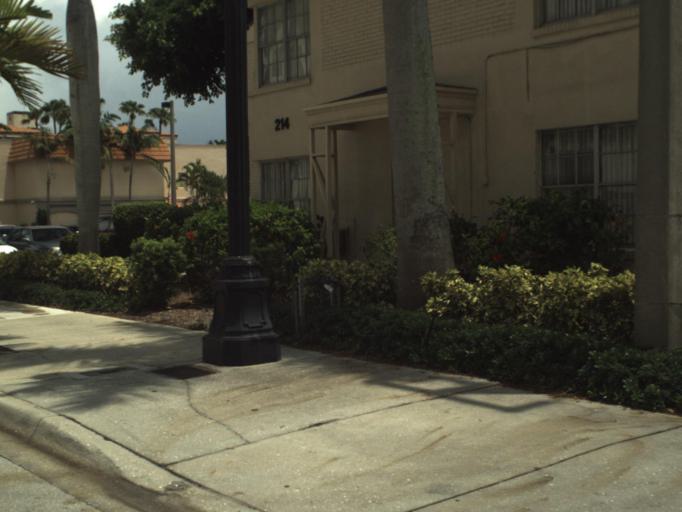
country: US
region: Florida
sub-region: Palm Beach County
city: West Palm Beach
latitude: 26.7054
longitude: -80.0513
